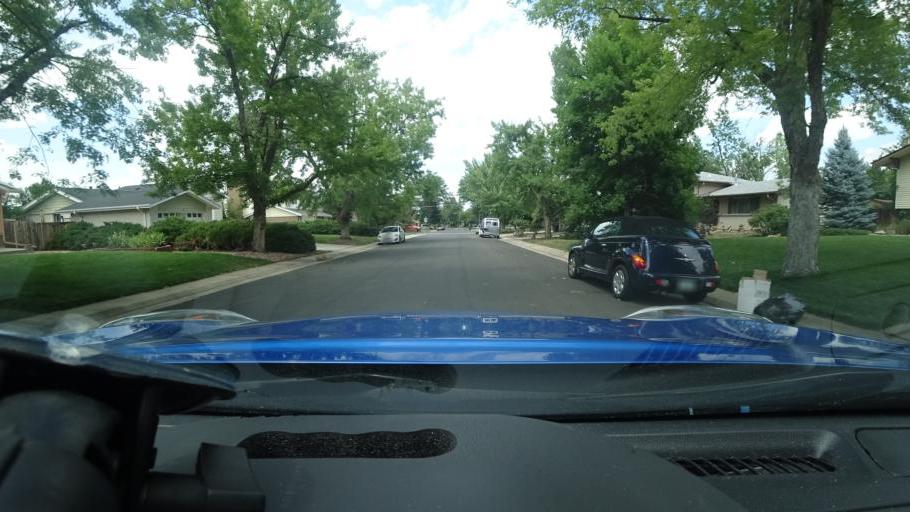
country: US
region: Colorado
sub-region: Adams County
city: Aurora
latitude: 39.7212
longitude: -104.8354
